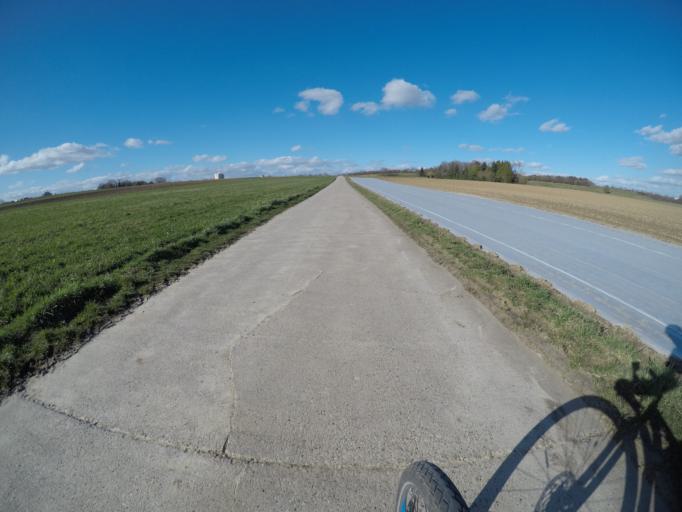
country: DE
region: Baden-Wuerttemberg
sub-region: Regierungsbezirk Stuttgart
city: Leinfelden-Echterdingen
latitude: 48.7029
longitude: 9.1591
